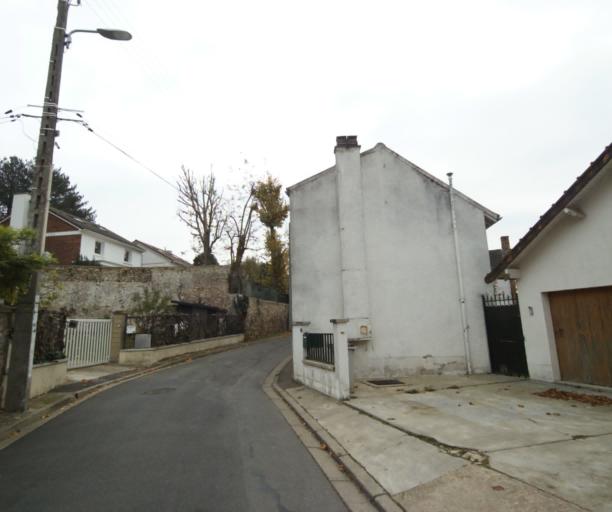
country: FR
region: Ile-de-France
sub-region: Departement des Yvelines
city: Triel-sur-Seine
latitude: 48.9901
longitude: 2.0055
